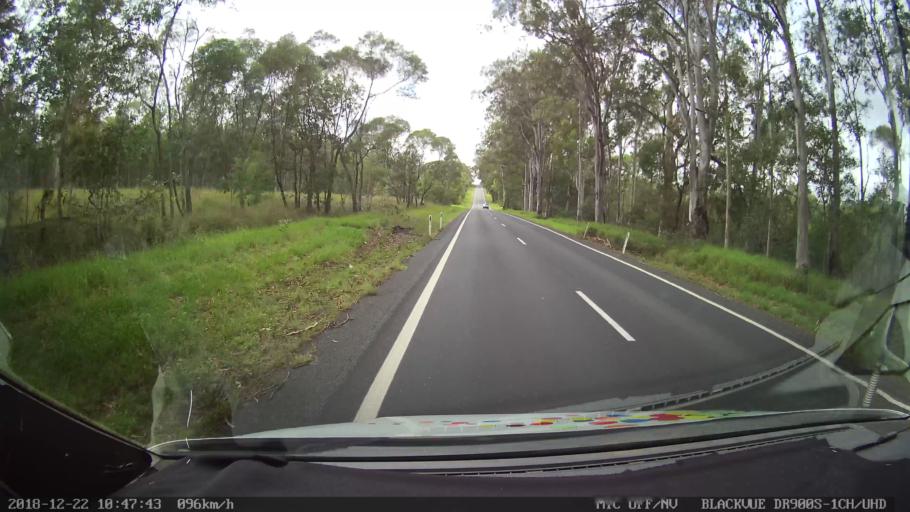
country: AU
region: New South Wales
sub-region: Clarence Valley
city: South Grafton
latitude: -29.6759
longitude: 152.8432
